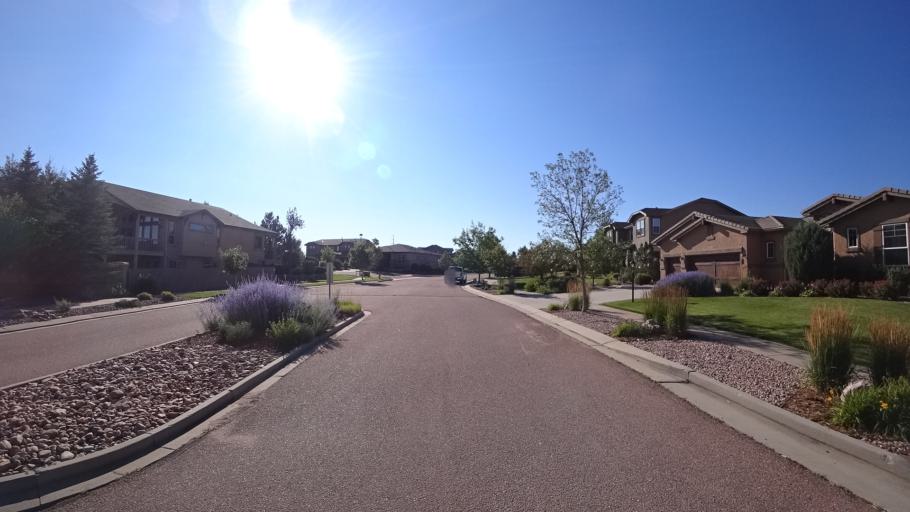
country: US
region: Colorado
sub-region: El Paso County
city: Black Forest
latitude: 38.9782
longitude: -104.7594
